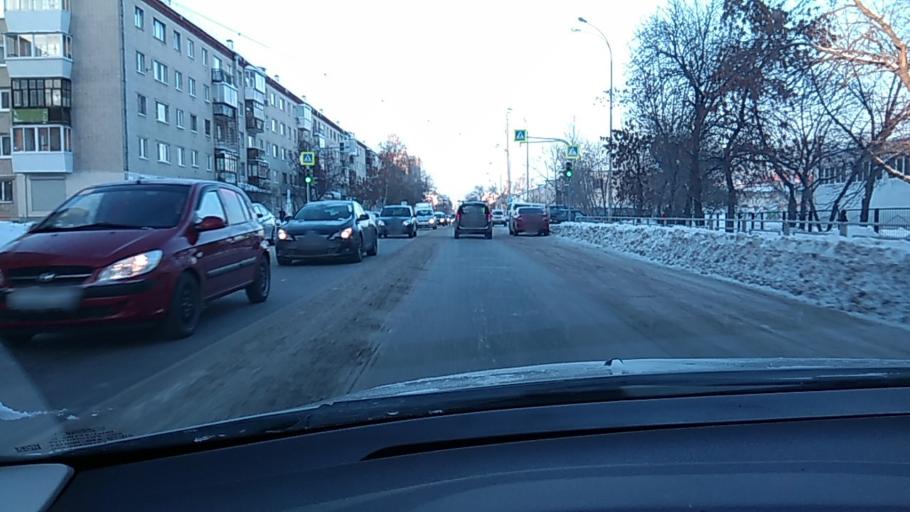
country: RU
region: Sverdlovsk
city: Yekaterinburg
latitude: 56.8104
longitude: 60.6125
